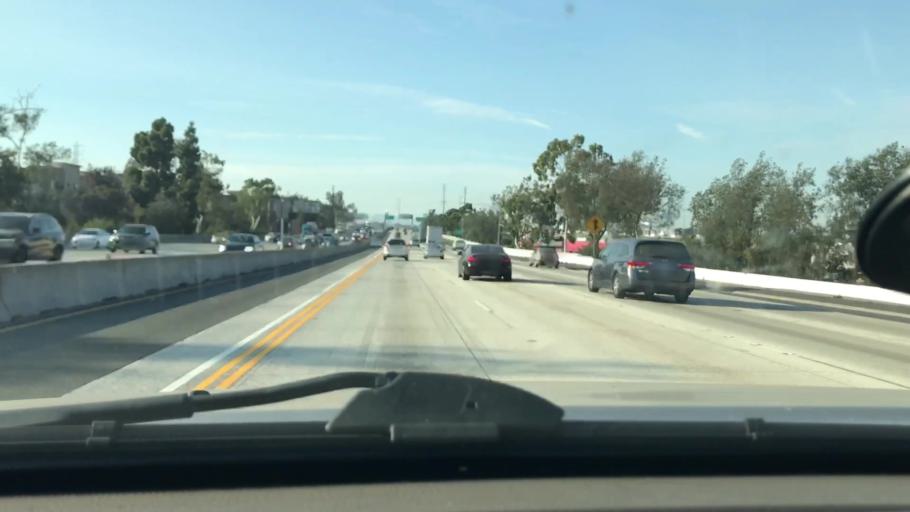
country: US
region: California
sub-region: Los Angeles County
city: Lawndale
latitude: 33.8922
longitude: -118.3630
